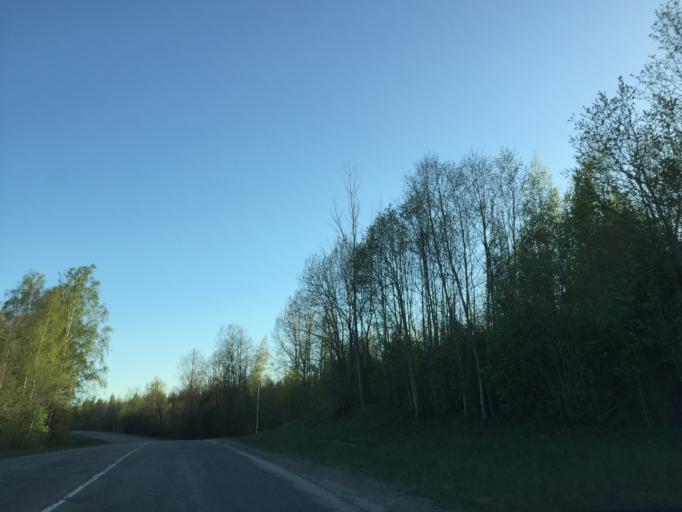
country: LV
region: Koknese
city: Koknese
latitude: 56.7021
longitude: 25.4888
